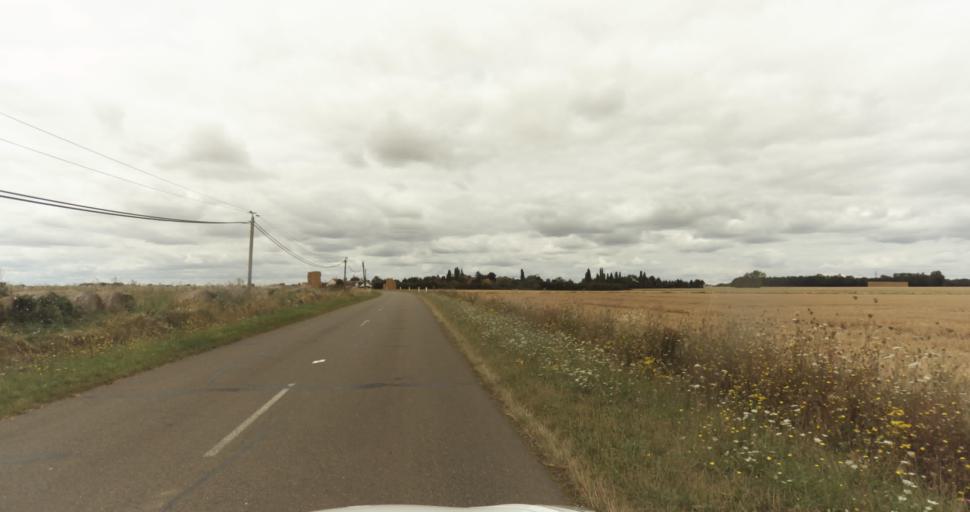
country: FR
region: Haute-Normandie
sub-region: Departement de l'Eure
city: La Madeleine-de-Nonancourt
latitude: 48.8328
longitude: 1.2079
